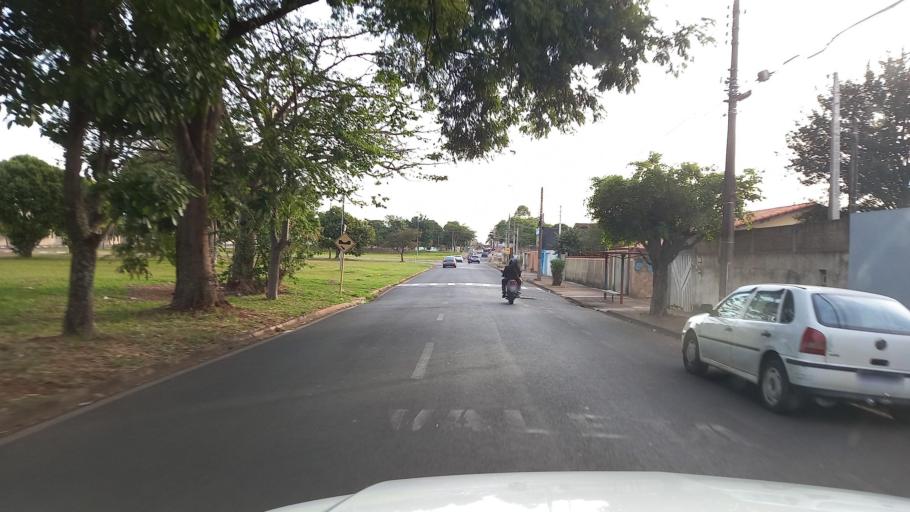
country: BR
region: Sao Paulo
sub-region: Moji-Guacu
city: Mogi-Gaucu
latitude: -22.3444
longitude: -46.9320
